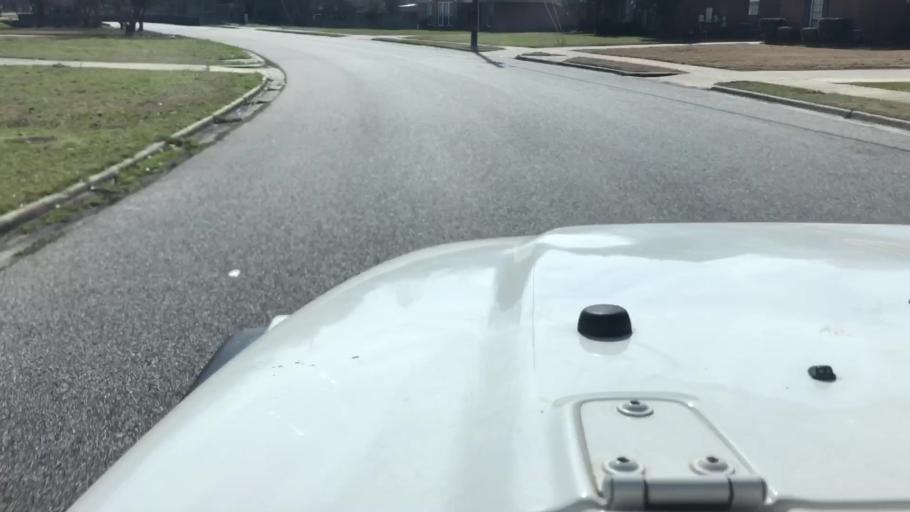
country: US
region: Alabama
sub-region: Elmore County
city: Blue Ridge
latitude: 32.4062
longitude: -86.1875
